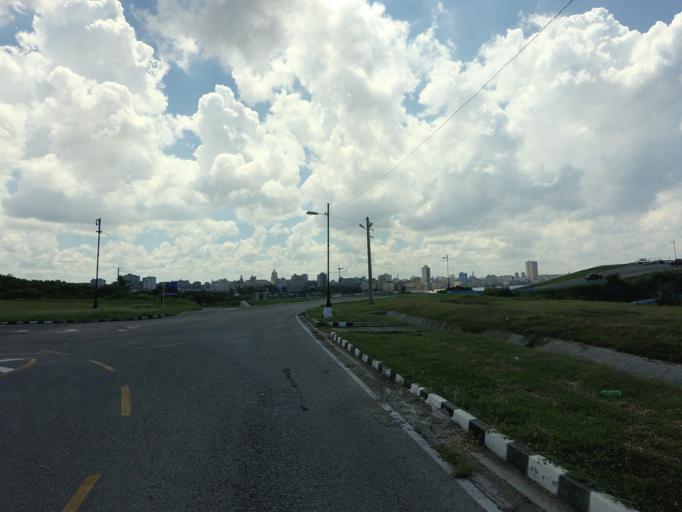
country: CU
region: La Habana
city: Centro Habana
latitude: 23.1507
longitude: -82.3541
